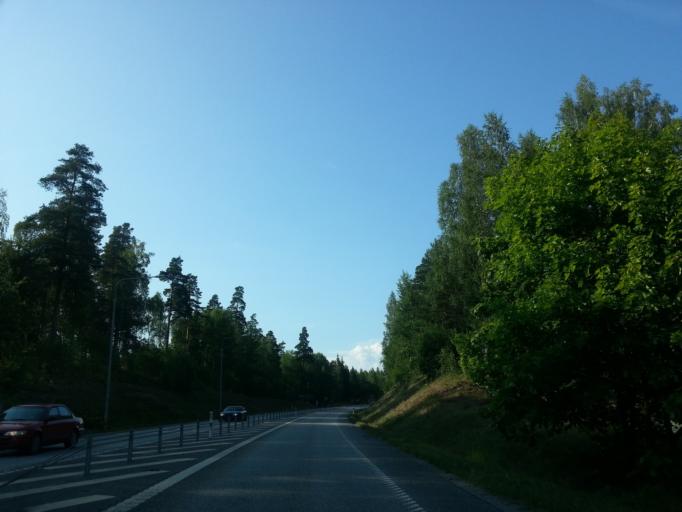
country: SE
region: Vaestmanland
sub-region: Fagersta Kommun
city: Fagersta
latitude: 60.0098
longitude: 15.7829
